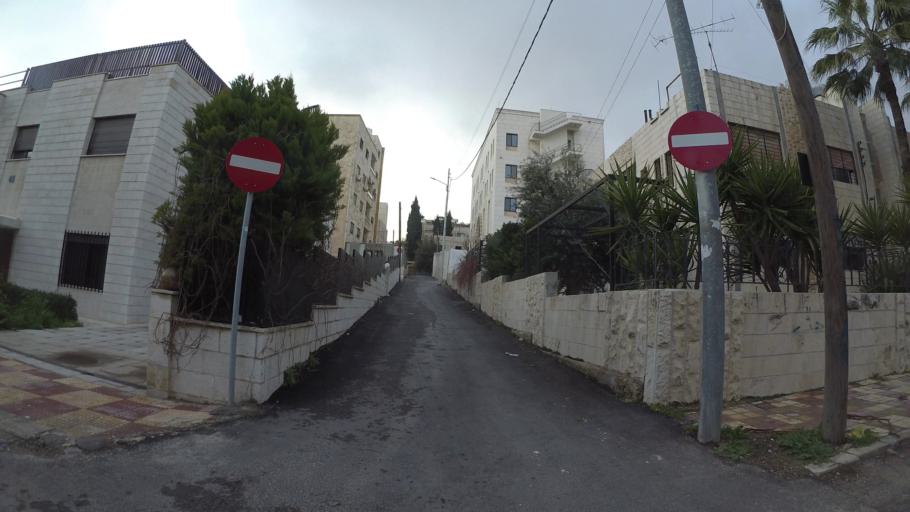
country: JO
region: Amman
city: Amman
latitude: 31.9620
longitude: 35.8876
